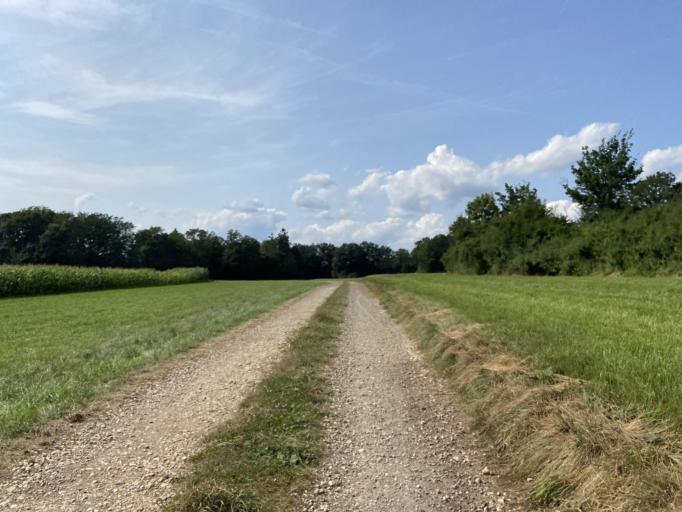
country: DE
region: Baden-Wuerttemberg
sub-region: Tuebingen Region
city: Scheer
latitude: 48.0821
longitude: 9.2826
